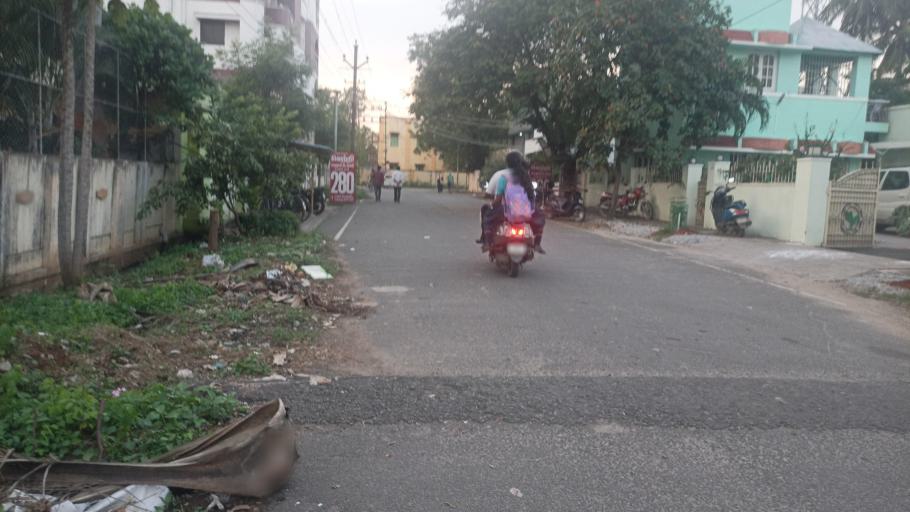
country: IN
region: Tamil Nadu
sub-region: Salem
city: Salem
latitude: 11.6741
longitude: 78.1208
